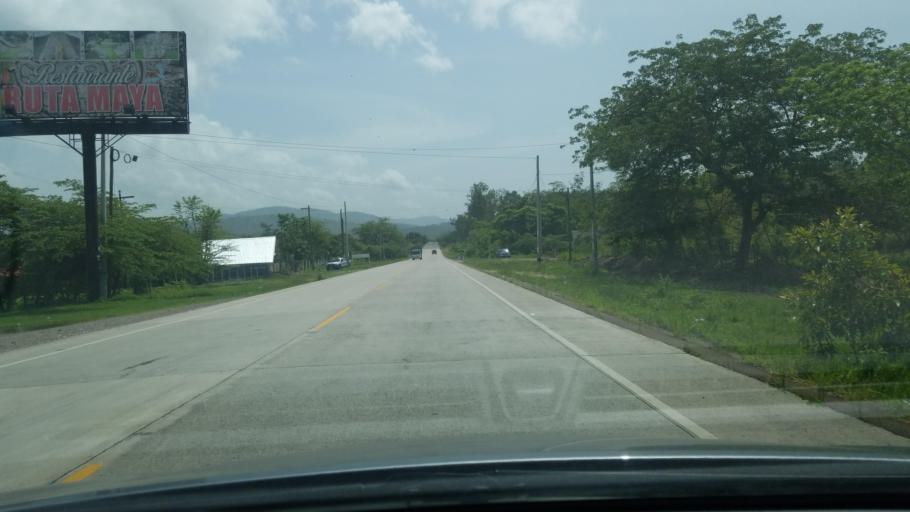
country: HN
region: Copan
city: Florida
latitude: 15.0573
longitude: -88.7967
